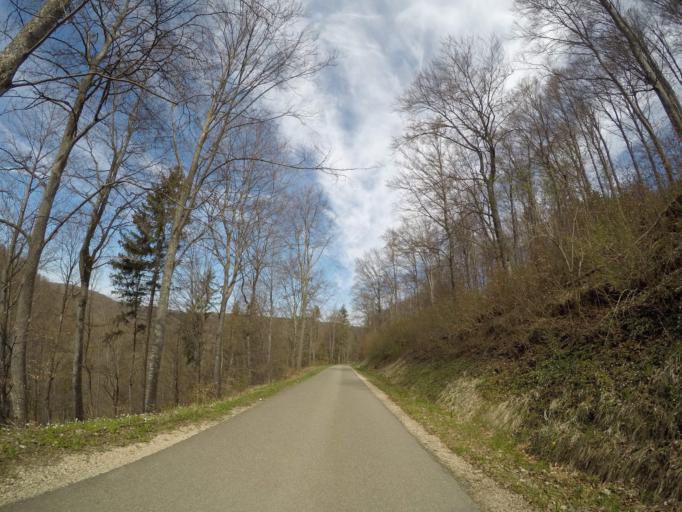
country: DE
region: Baden-Wuerttemberg
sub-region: Tuebingen Region
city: Mehrstetten
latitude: 48.3631
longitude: 9.6225
